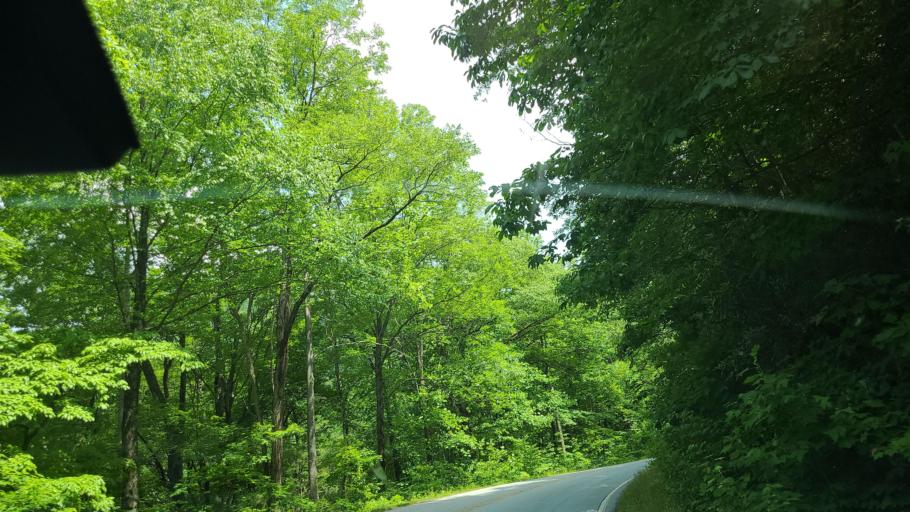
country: US
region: Georgia
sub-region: Rabun County
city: Mountain City
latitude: 35.0259
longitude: -83.1861
